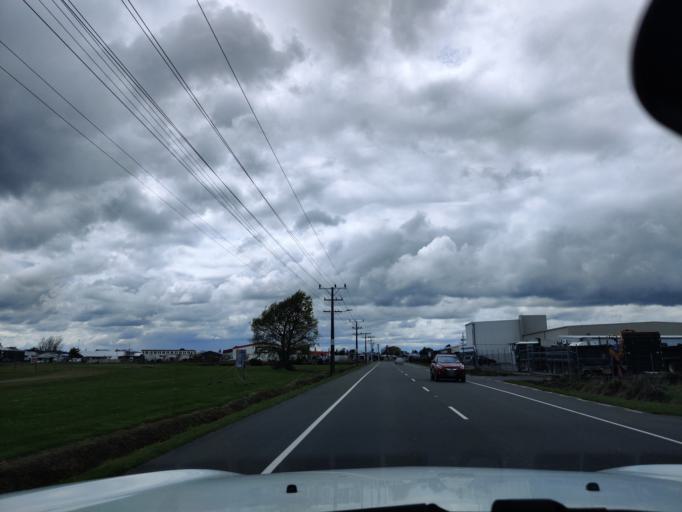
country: NZ
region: Manawatu-Wanganui
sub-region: Palmerston North City
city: Palmerston North
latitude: -40.2329
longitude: 175.5660
